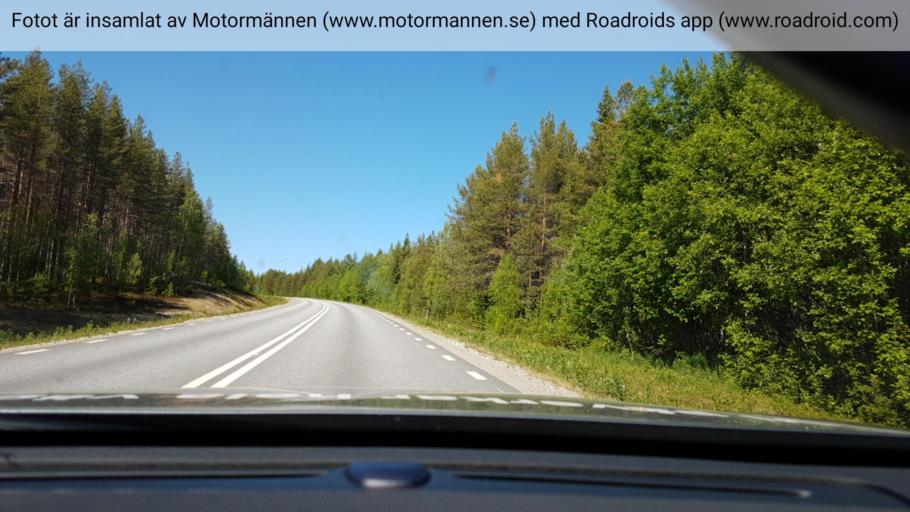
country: SE
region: Vaesterbotten
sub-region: Asele Kommun
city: Insjon
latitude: 64.2008
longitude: 17.6508
